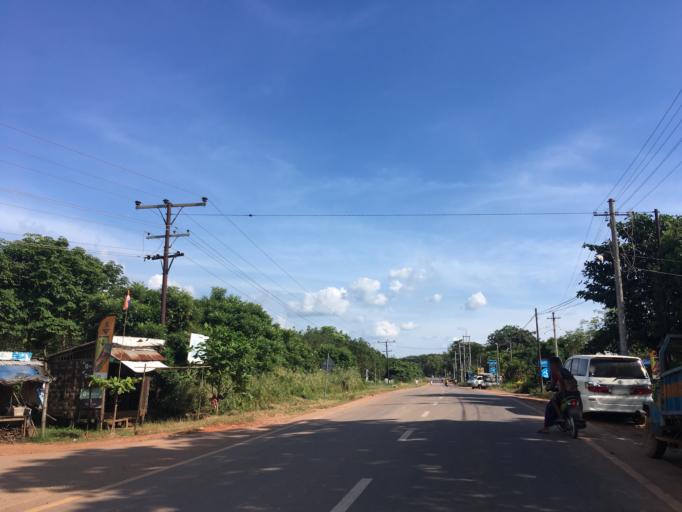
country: MM
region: Mon
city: Mawlamyine
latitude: 16.4579
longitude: 97.6734
